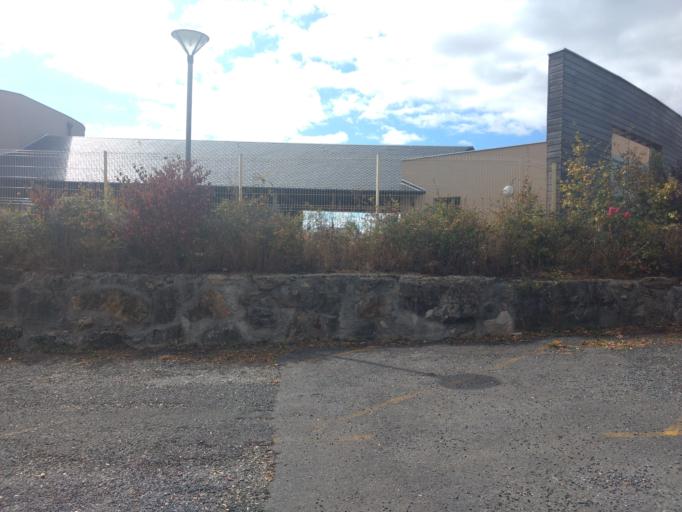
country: FR
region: Midi-Pyrenees
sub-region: Departement de l'Aveyron
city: Olemps
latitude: 44.3557
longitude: 2.5572
